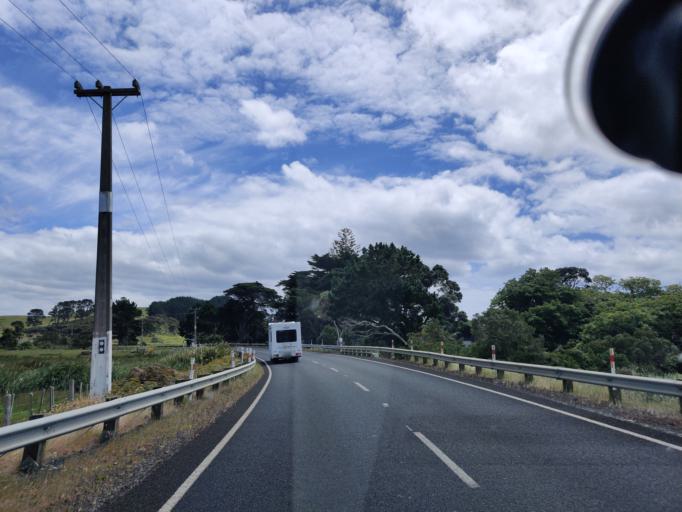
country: NZ
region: Northland
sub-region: Far North District
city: Kaitaia
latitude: -34.7605
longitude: 173.0763
